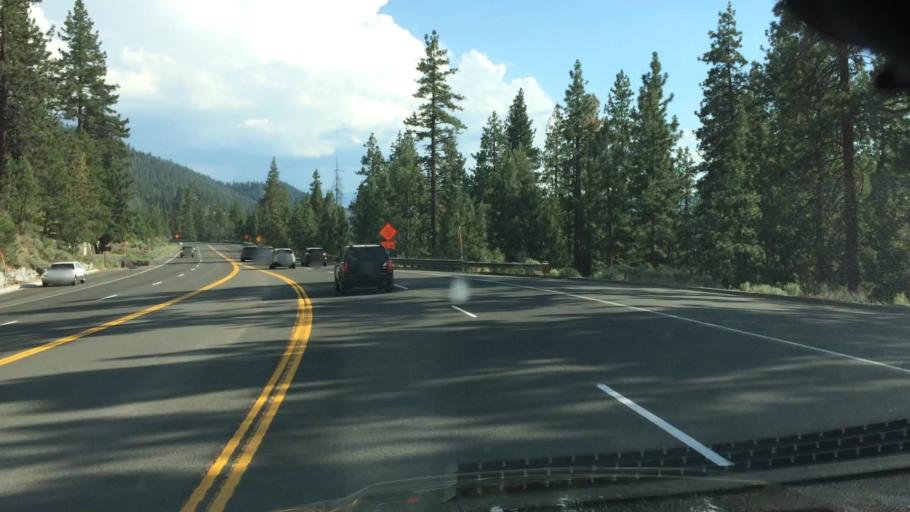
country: US
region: Nevada
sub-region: Douglas County
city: Kingsbury
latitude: 39.0806
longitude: -119.9428
